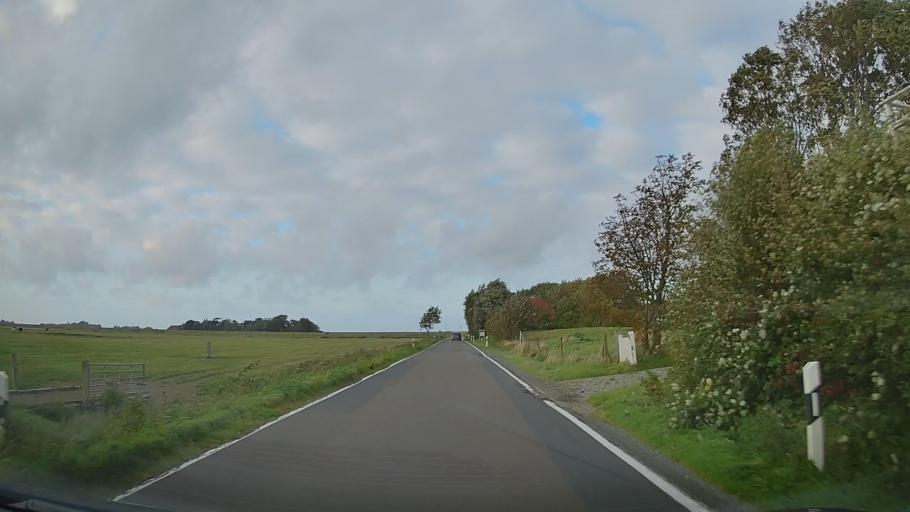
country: DE
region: Schleswig-Holstein
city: Osterhever
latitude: 54.3838
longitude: 8.7588
